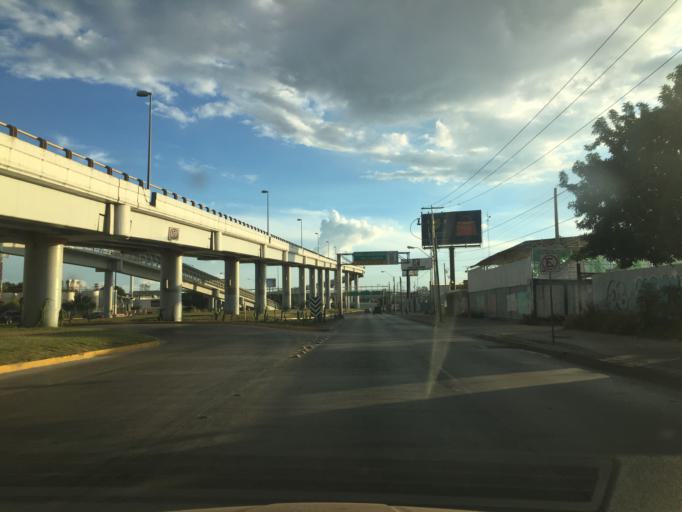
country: MX
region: Guanajuato
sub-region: Leon
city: Fraccionamiento Paraiso Real
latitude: 21.0996
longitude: -101.6258
